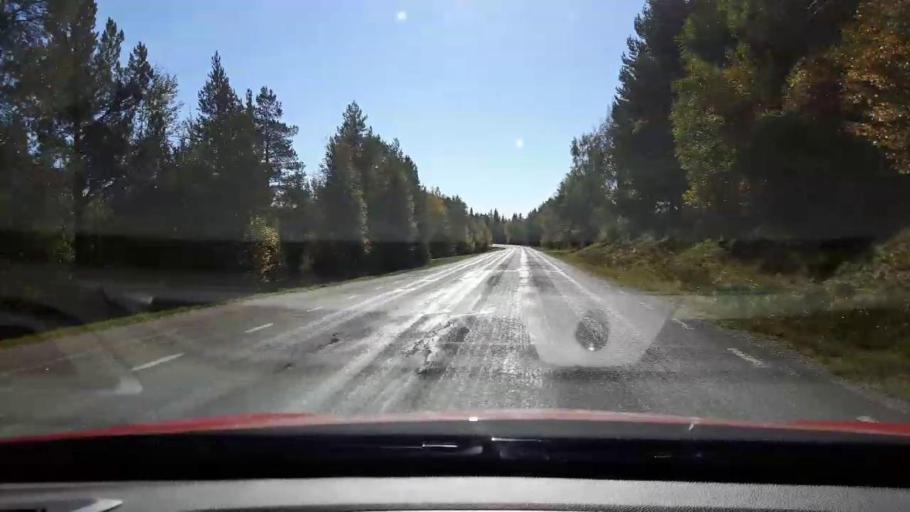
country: SE
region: Jaemtland
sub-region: Harjedalens Kommun
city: Sveg
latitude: 62.3423
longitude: 14.0379
